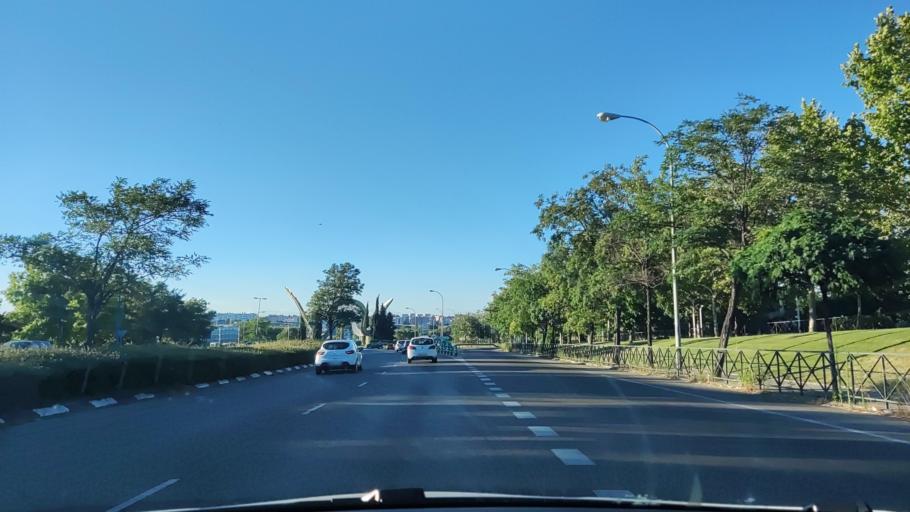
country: ES
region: Madrid
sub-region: Provincia de Madrid
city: Leganes
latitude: 40.3452
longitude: -3.7555
